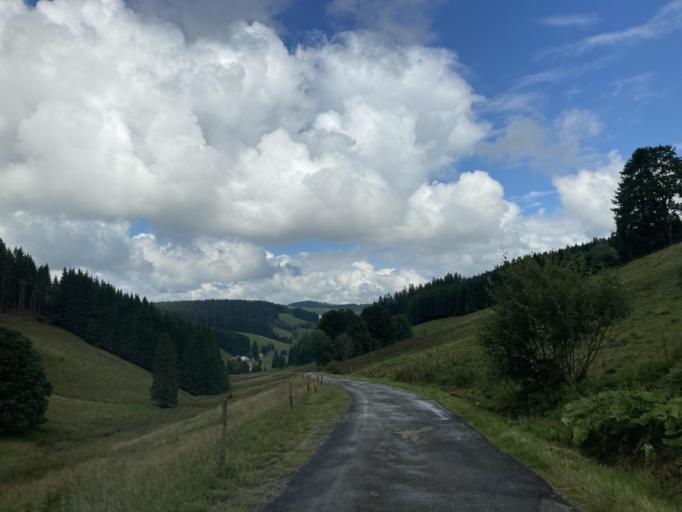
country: DE
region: Baden-Wuerttemberg
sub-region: Freiburg Region
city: Furtwangen im Schwarzwald
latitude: 48.0248
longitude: 8.1896
